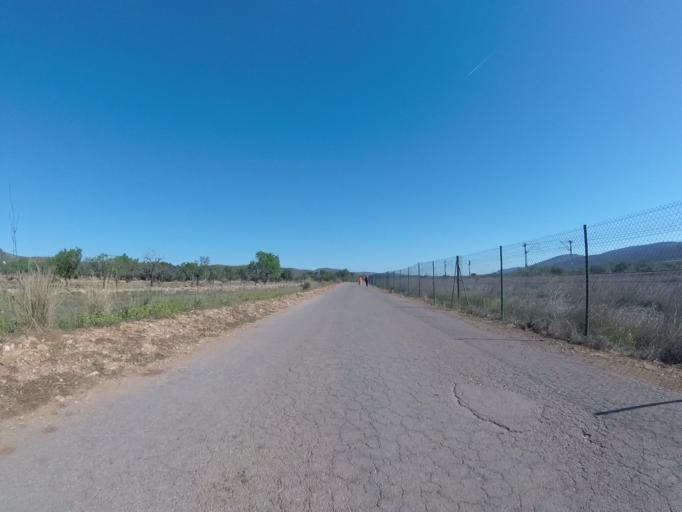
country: ES
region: Valencia
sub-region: Provincia de Castello
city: Alcala de Xivert
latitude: 40.3200
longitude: 0.2352
